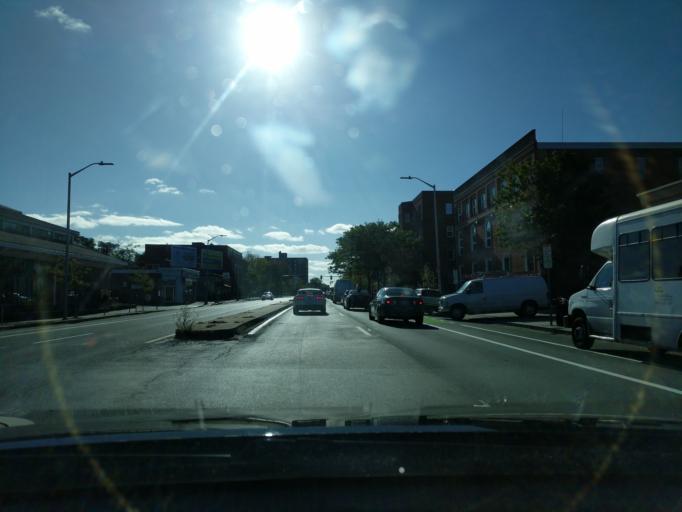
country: US
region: Massachusetts
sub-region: Middlesex County
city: Arlington
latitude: 42.3989
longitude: -71.1321
